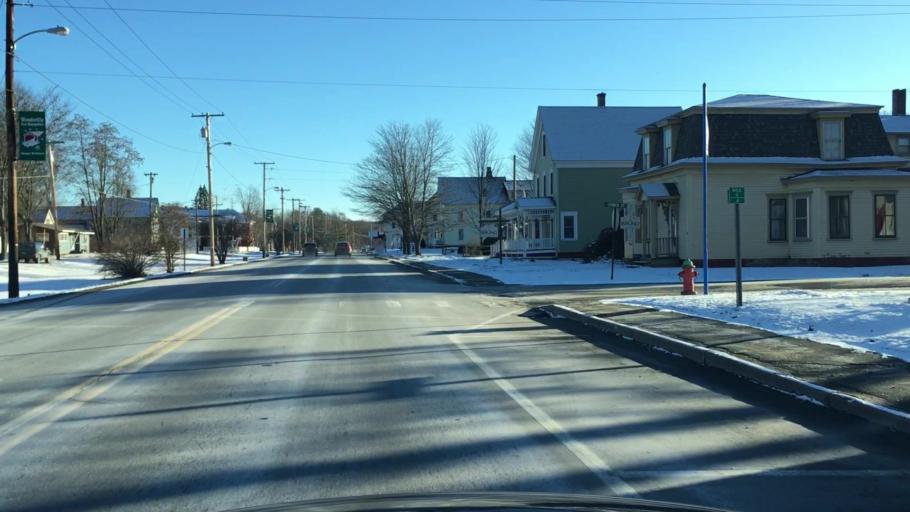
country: US
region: New Hampshire
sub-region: Grafton County
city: Woodsville
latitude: 44.1504
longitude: -72.0355
